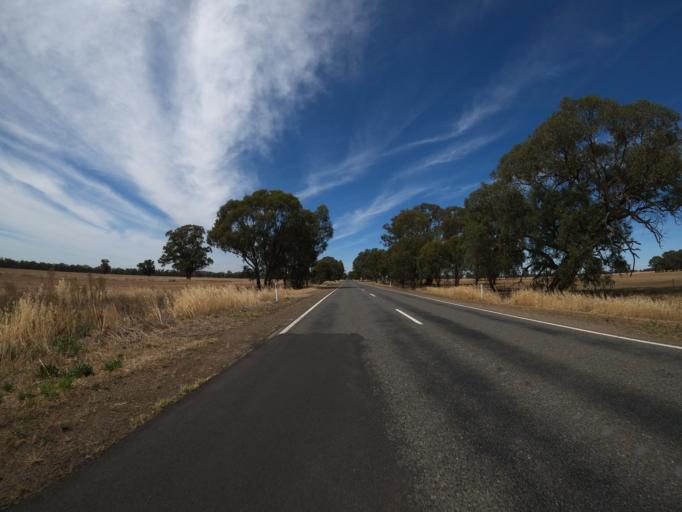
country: AU
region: Victoria
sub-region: Moira
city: Yarrawonga
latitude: -36.2831
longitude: 145.9523
